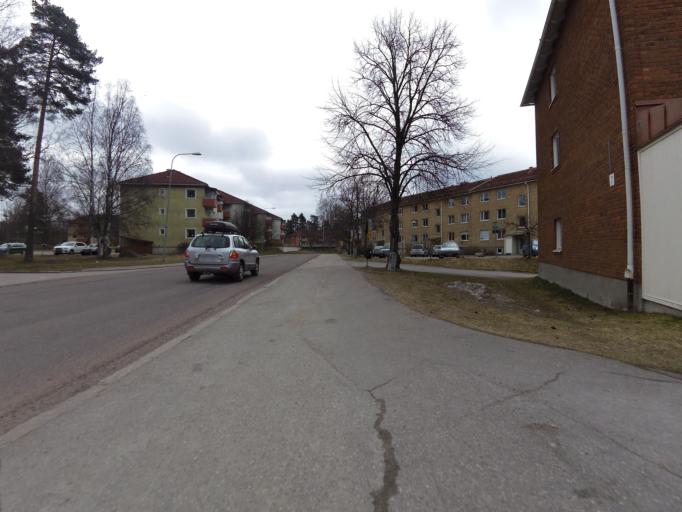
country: SE
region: Gaevleborg
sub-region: Hofors Kommun
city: Hofors
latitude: 60.5430
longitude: 16.2738
